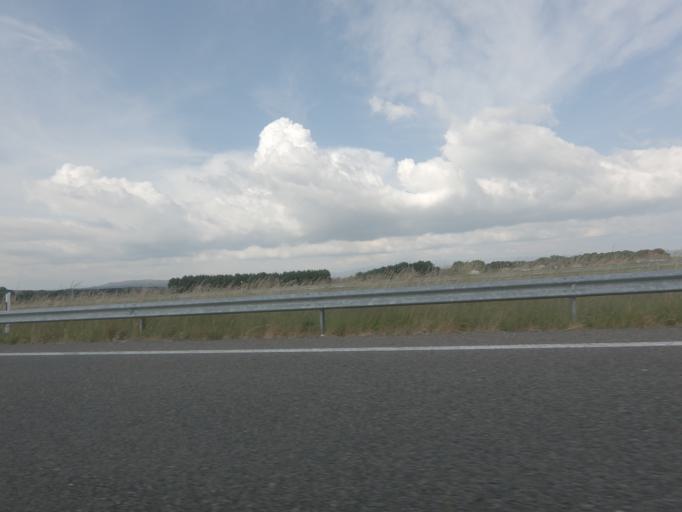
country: ES
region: Galicia
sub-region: Provincia de Ourense
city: Ambia
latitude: 42.1379
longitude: -7.7444
